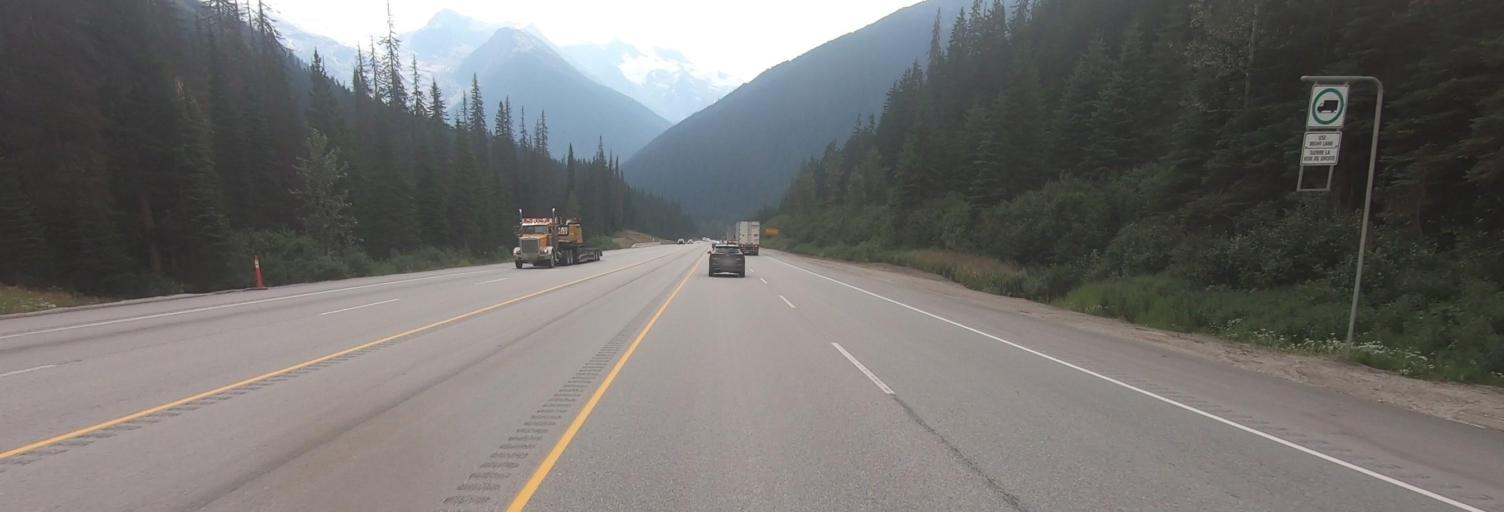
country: CA
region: British Columbia
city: Golden
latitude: 51.2809
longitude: -117.5127
